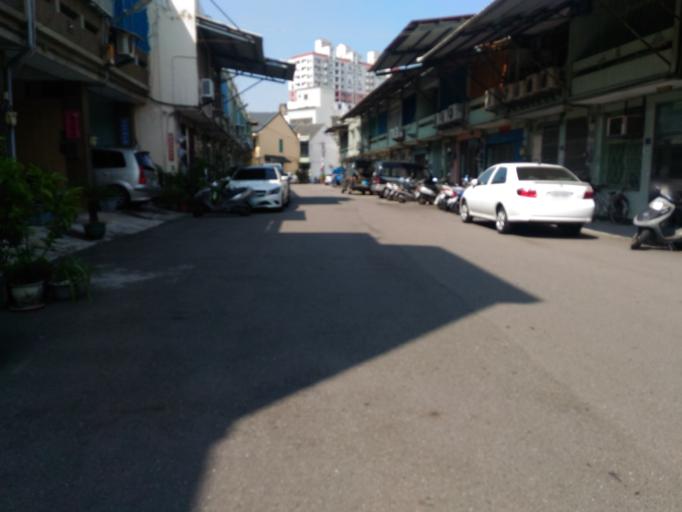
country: TW
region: Taiwan
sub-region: Changhua
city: Chang-hua
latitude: 24.0826
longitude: 120.5522
